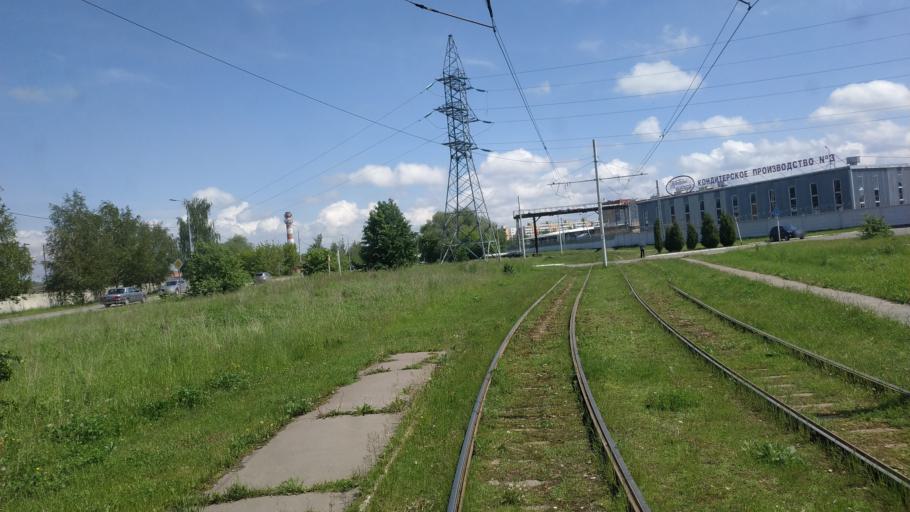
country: RU
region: Moskovskaya
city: Sychevo
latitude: 55.0600
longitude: 38.7324
